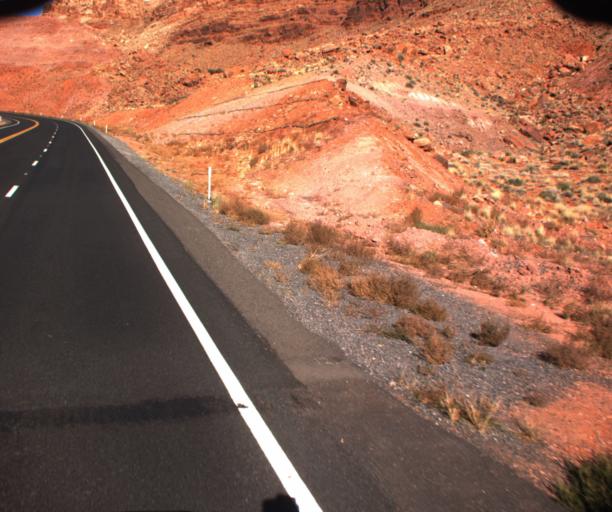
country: US
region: Arizona
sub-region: Coconino County
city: LeChee
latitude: 36.6491
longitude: -111.6328
